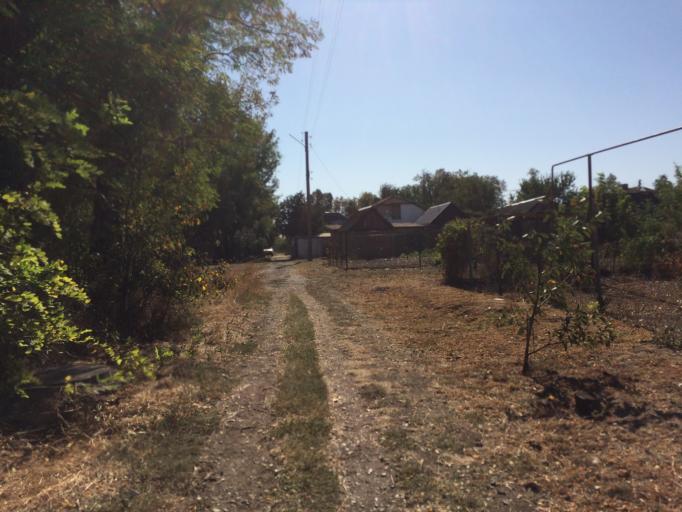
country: RU
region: Rostov
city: Gigant
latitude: 46.5170
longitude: 41.1878
